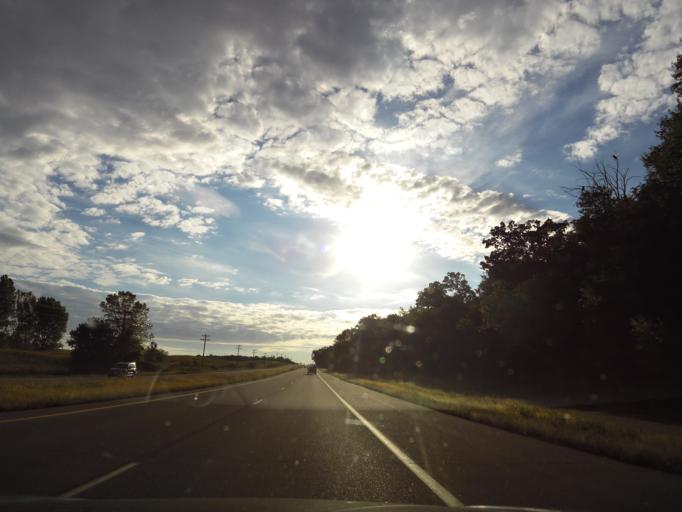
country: US
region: Minnesota
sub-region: Scott County
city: Prior Lake
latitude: 44.7466
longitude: -93.4206
